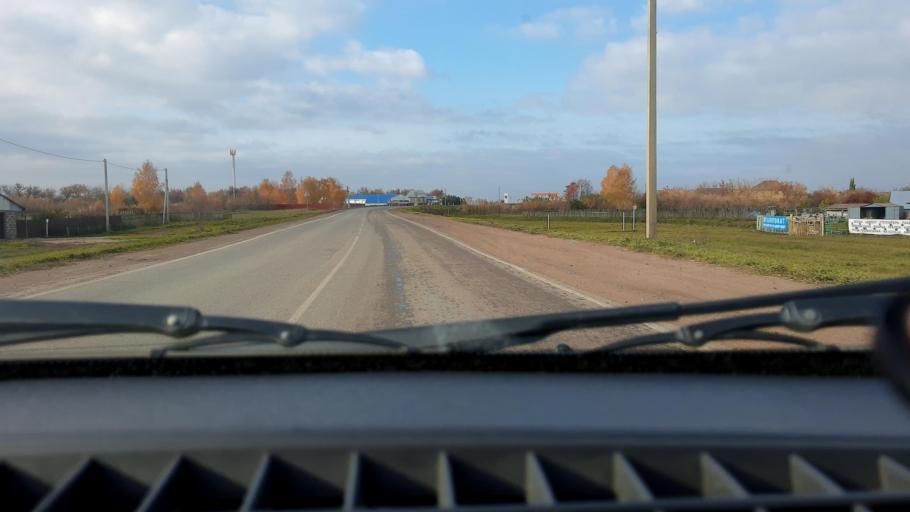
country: RU
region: Bashkortostan
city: Kabakovo
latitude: 54.5487
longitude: 56.0937
